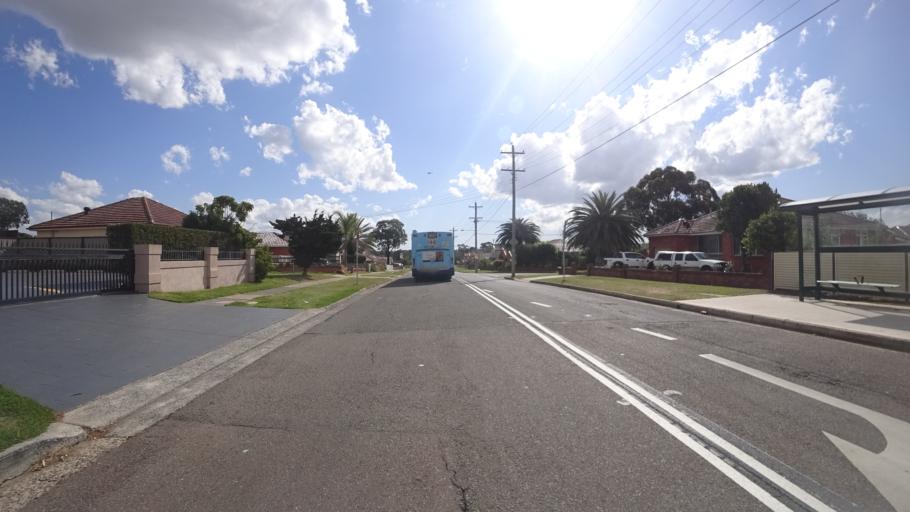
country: AU
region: New South Wales
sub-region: Liverpool
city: Miller
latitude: -33.9229
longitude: 150.9079
